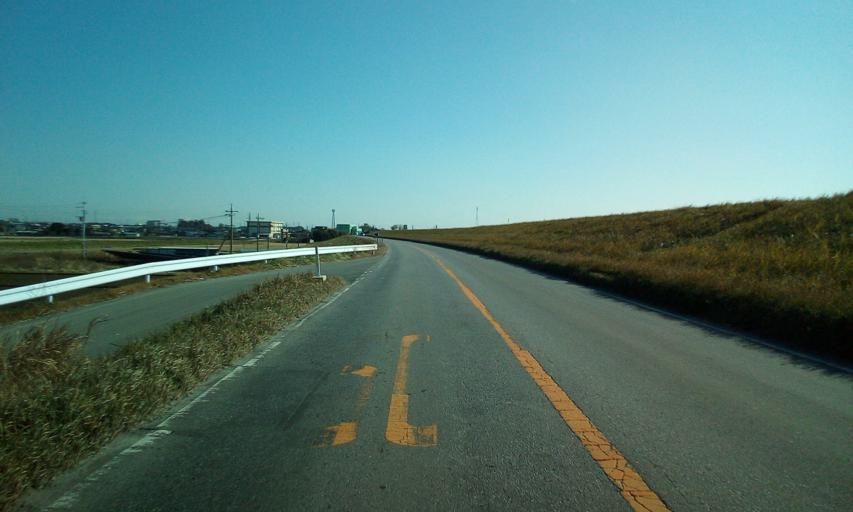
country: JP
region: Ibaraki
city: Sakai
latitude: 36.1125
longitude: 139.7787
